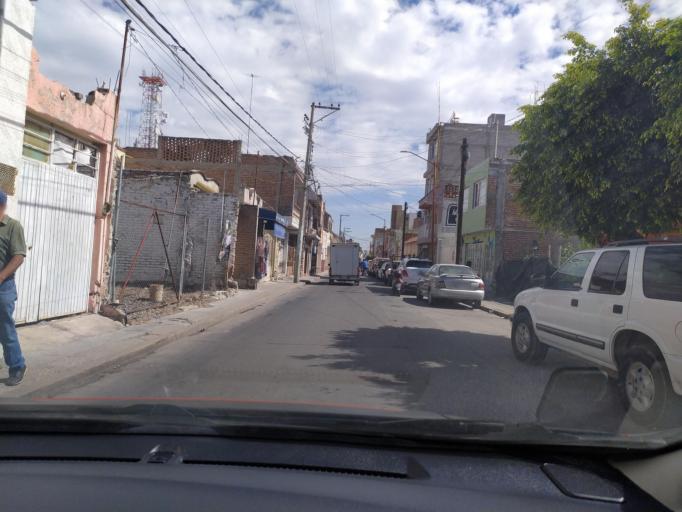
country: LA
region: Oudomxai
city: Muang La
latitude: 21.0171
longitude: 101.8606
